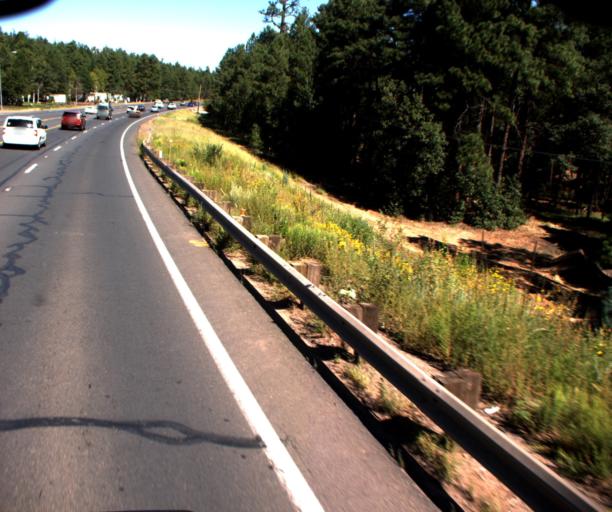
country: US
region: Arizona
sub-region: Navajo County
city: Show Low
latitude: 34.2125
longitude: -110.0273
